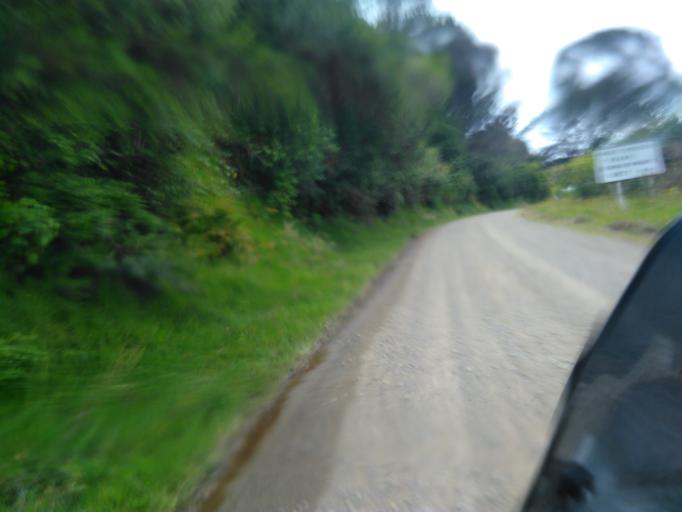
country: NZ
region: Bay of Plenty
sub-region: Opotiki District
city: Opotiki
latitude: -38.0253
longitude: 177.4379
